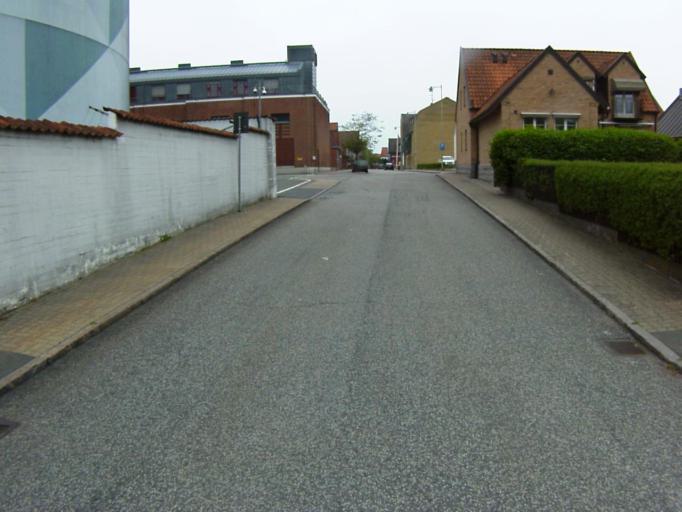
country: SE
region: Skane
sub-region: Kristianstads Kommun
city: Ahus
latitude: 55.9242
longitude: 14.3002
